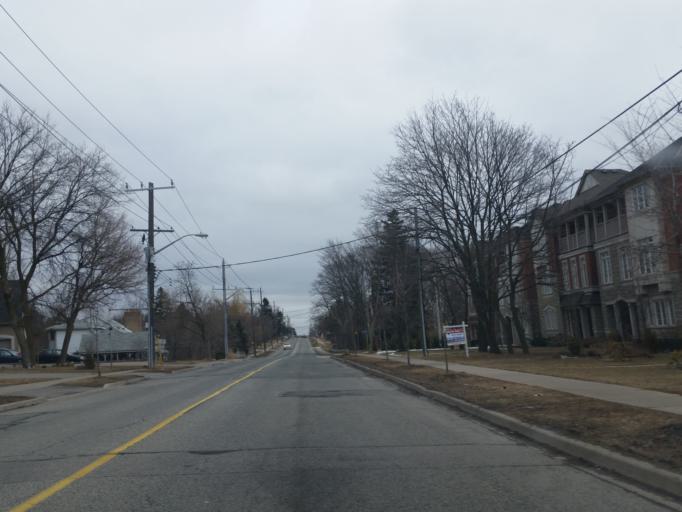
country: CA
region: Ontario
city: Scarborough
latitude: 43.7890
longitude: -79.1617
